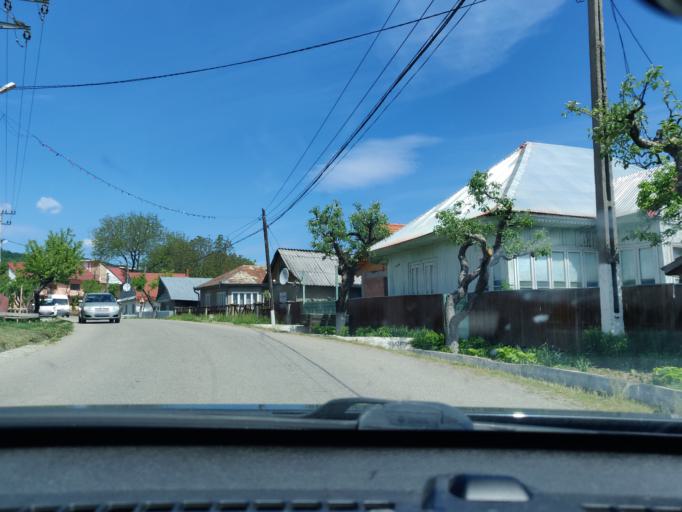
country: RO
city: Vizantea-Manastireasca
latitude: 45.9879
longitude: 26.7756
